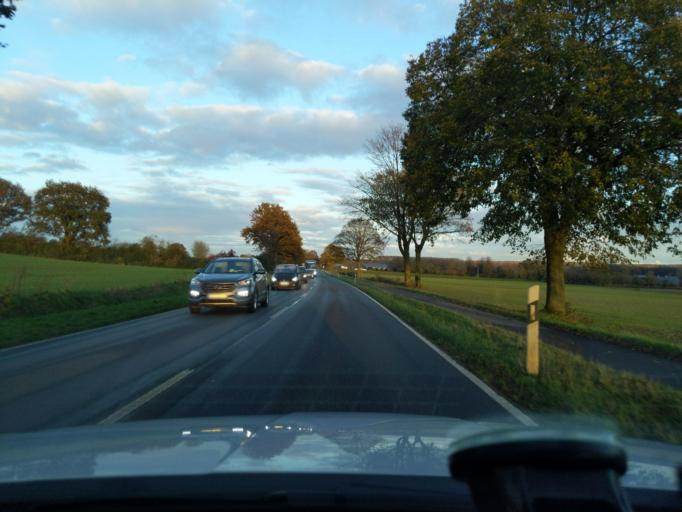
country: DE
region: North Rhine-Westphalia
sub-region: Regierungsbezirk Dusseldorf
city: Uedem
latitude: 51.6726
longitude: 6.2991
